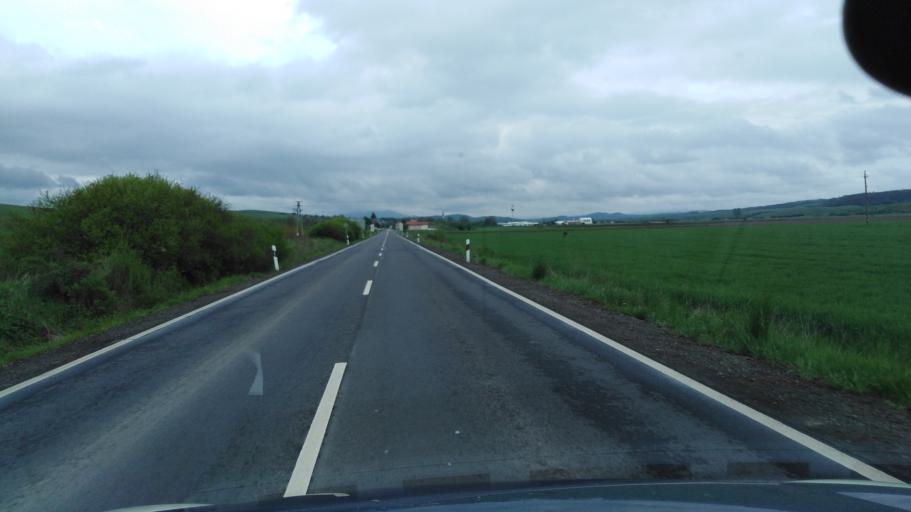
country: HU
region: Nograd
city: Szecseny
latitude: 48.1252
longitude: 19.5581
